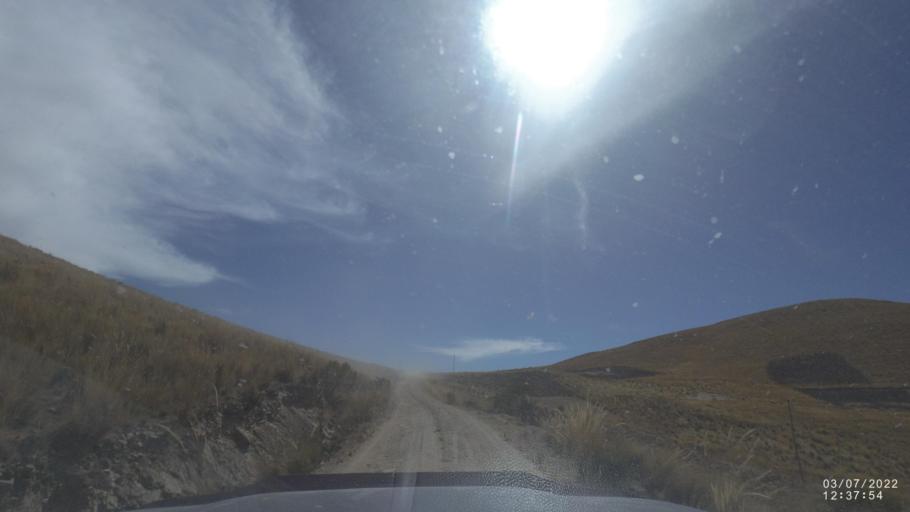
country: BO
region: Cochabamba
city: Irpa Irpa
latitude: -17.7954
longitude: -66.6169
